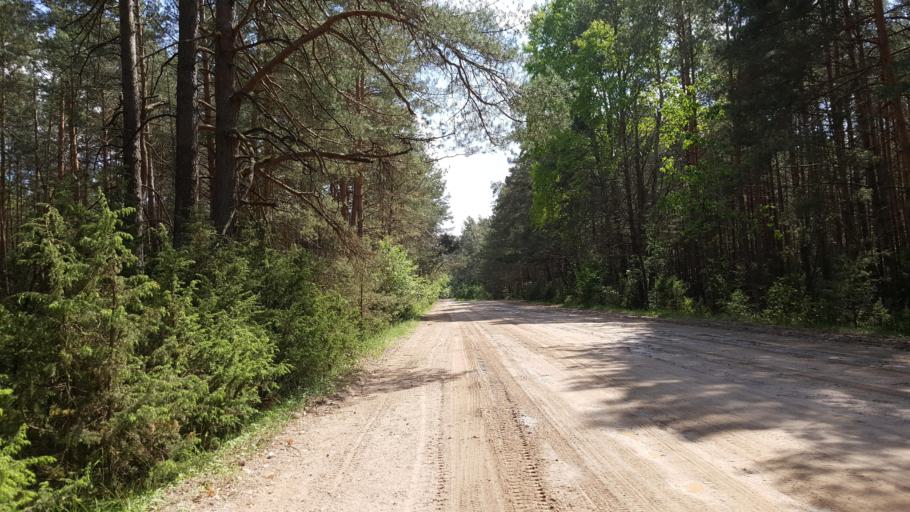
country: BY
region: Brest
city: Kamyanyets
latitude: 52.4321
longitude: 23.9724
